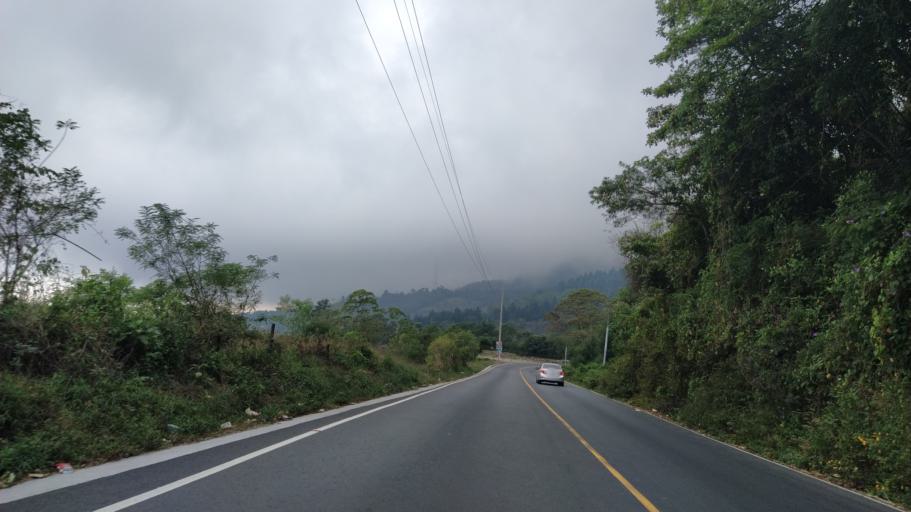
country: GT
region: Quetzaltenango
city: Zunil
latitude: 14.7302
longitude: -91.5221
